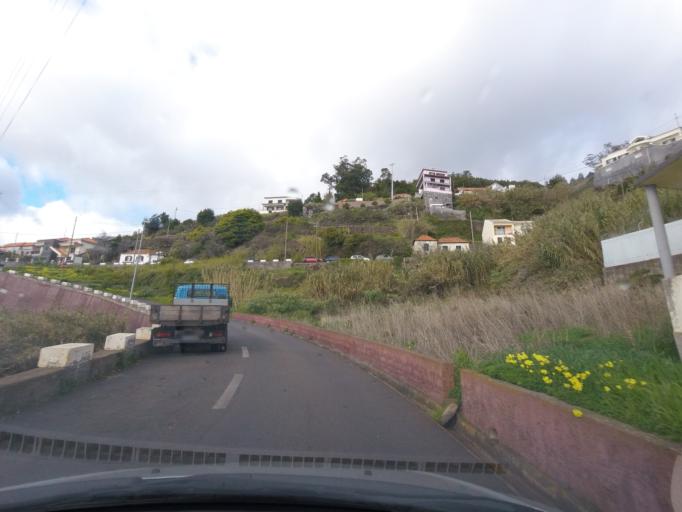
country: PT
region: Madeira
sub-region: Ribeira Brava
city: Campanario
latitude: 32.6625
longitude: -17.0193
